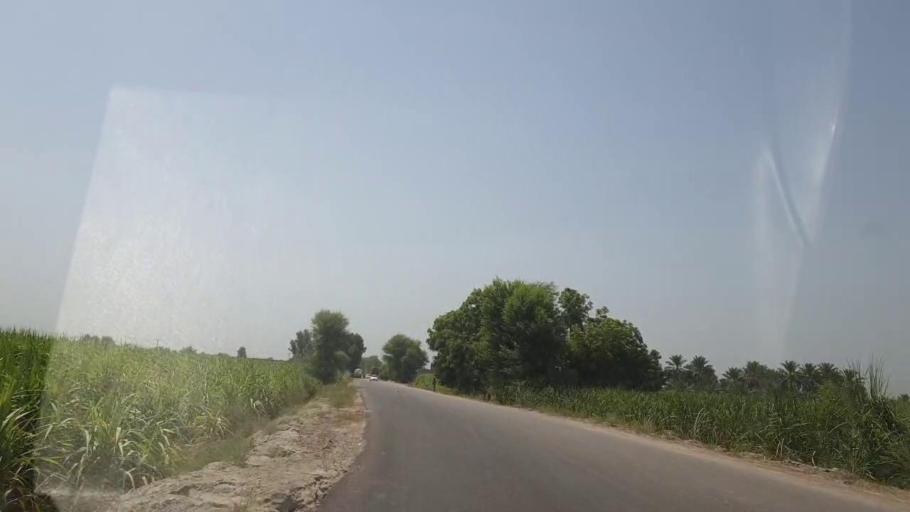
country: PK
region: Sindh
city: Ranipur
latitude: 27.2927
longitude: 68.6045
